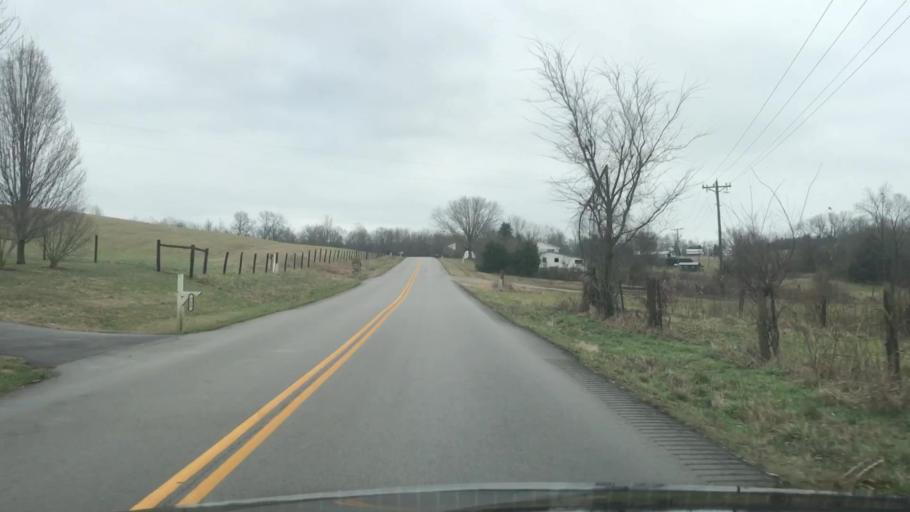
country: US
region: Kentucky
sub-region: Barren County
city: Glasgow
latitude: 36.9128
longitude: -85.8014
